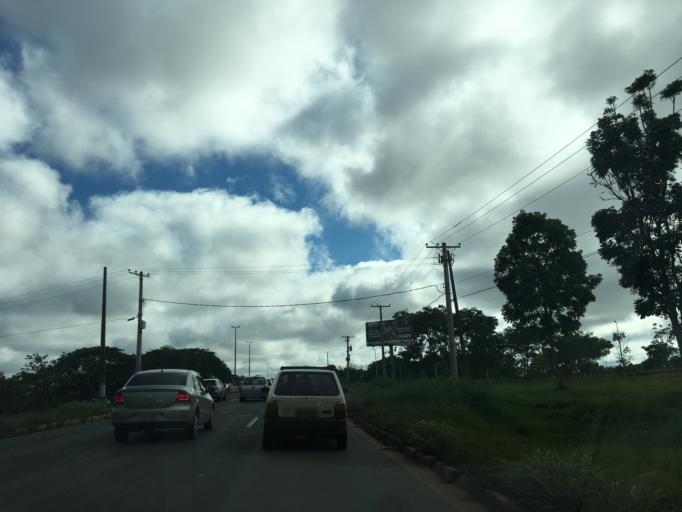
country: BR
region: Federal District
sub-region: Brasilia
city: Brasilia
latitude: -15.8673
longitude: -47.9446
